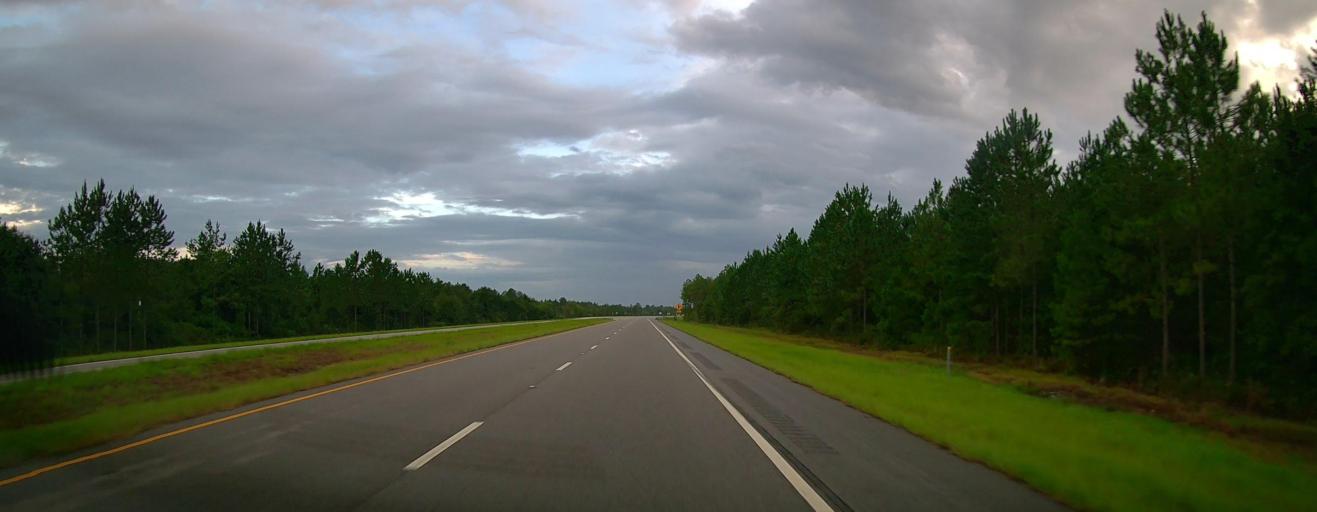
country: US
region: Georgia
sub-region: Ware County
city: Deenwood
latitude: 31.1656
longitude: -82.4149
